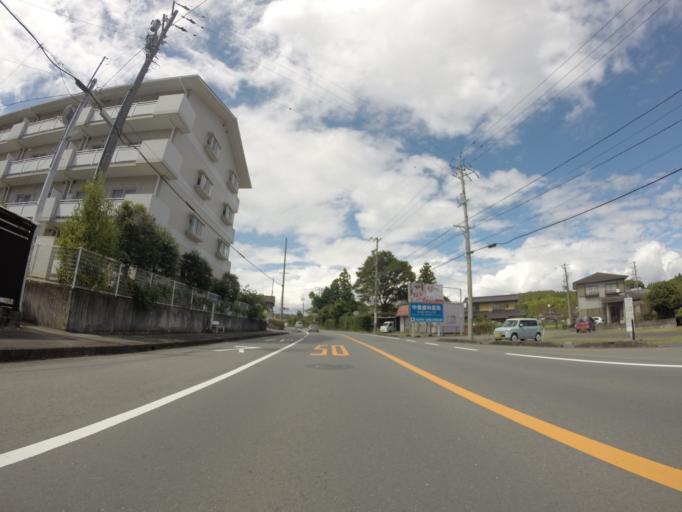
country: JP
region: Shizuoka
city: Kakegawa
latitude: 34.7466
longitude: 138.0399
